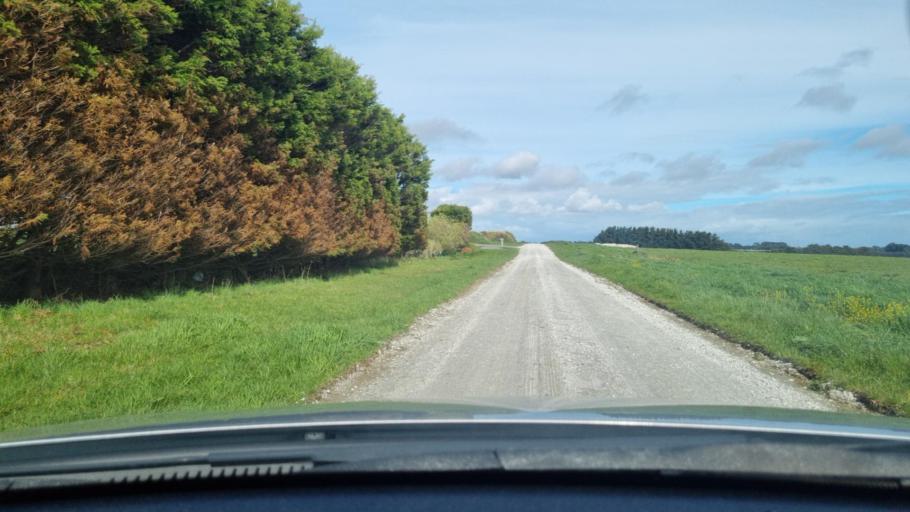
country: NZ
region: Southland
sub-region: Invercargill City
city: Invercargill
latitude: -46.4548
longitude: 168.3851
